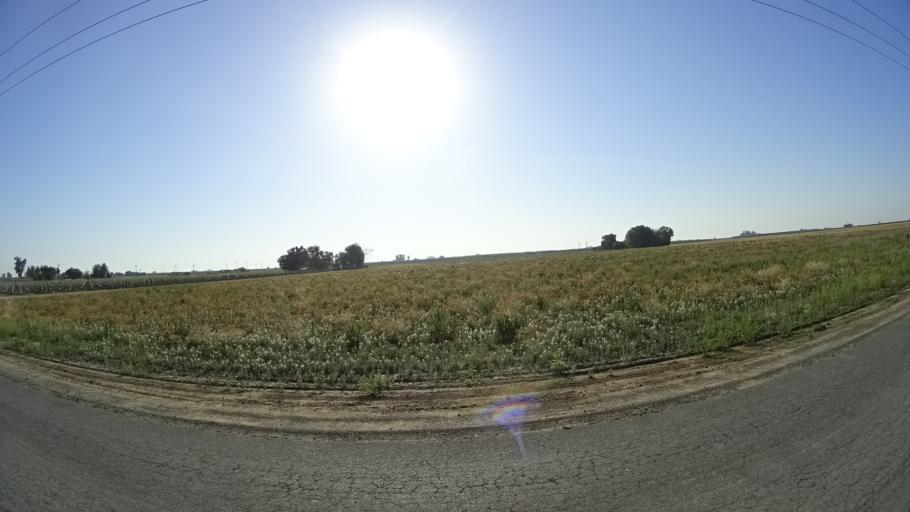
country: US
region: California
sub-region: Kings County
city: Lemoore
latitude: 36.2672
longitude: -119.7446
